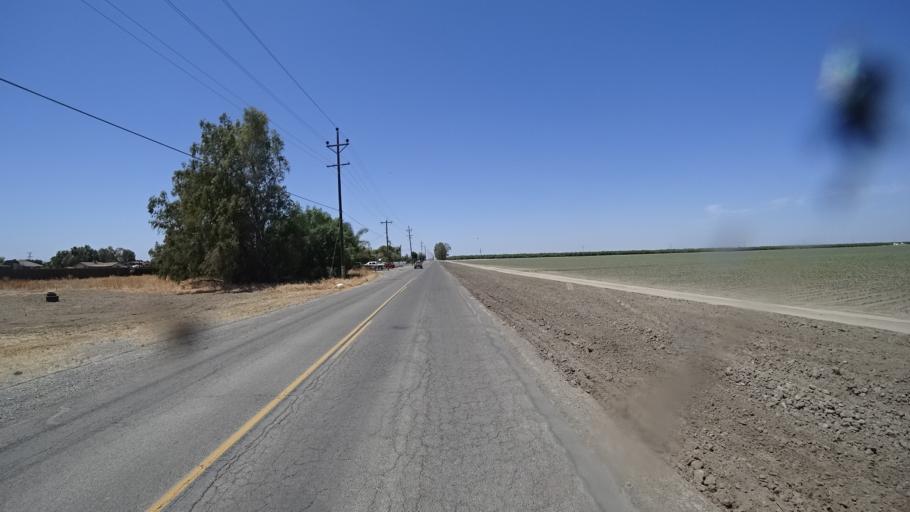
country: US
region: California
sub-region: Kings County
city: Corcoran
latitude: 36.1088
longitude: -119.5859
